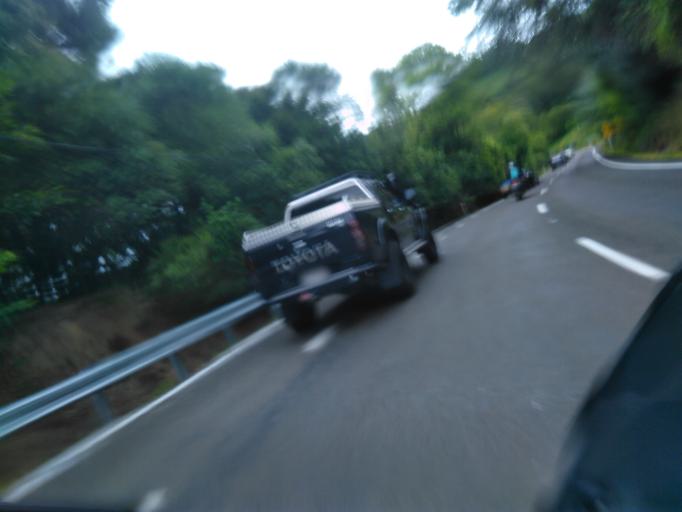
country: NZ
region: Gisborne
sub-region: Gisborne District
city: Gisborne
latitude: -38.4738
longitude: 177.6764
